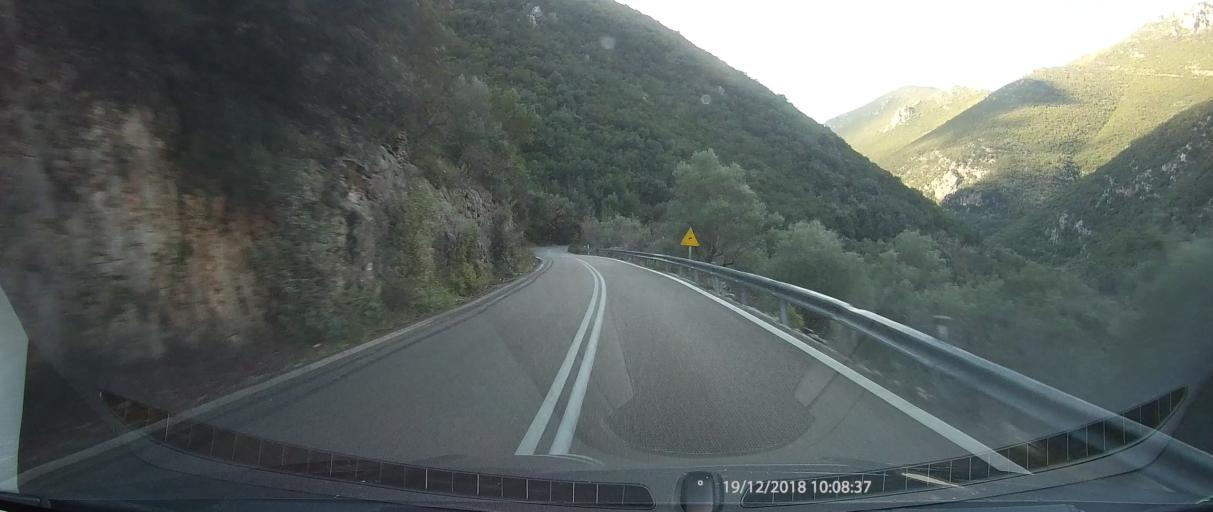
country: GR
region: Peloponnese
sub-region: Nomos Messinias
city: Kalamata
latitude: 37.1142
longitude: 22.1999
